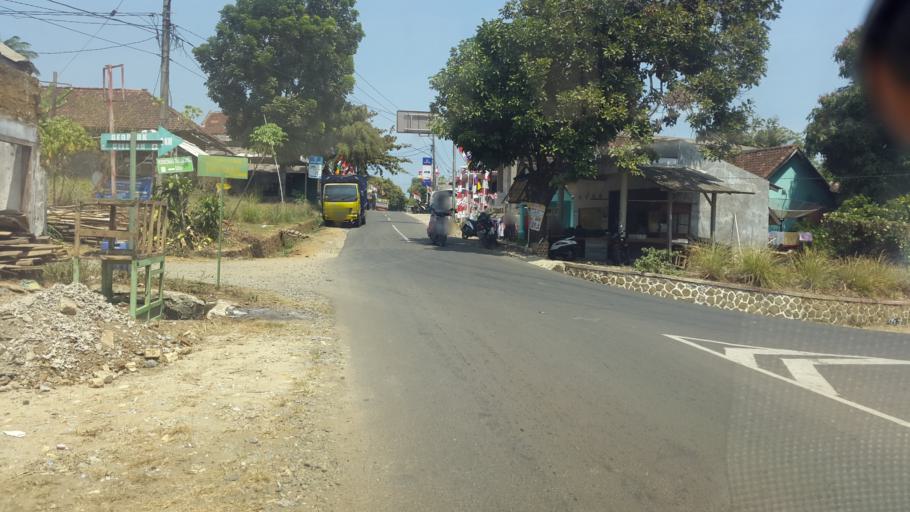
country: ID
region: West Java
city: Ciemas
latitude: -7.2326
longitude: 106.5222
